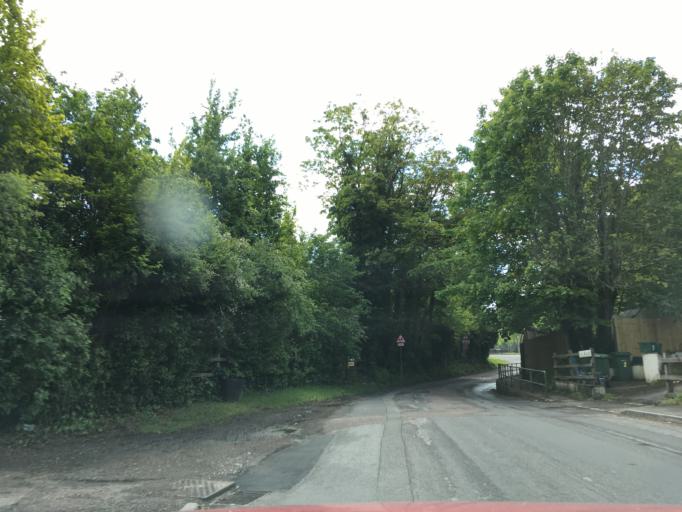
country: GB
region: England
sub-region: Gloucestershire
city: Dursley
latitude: 51.6906
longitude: -2.3555
